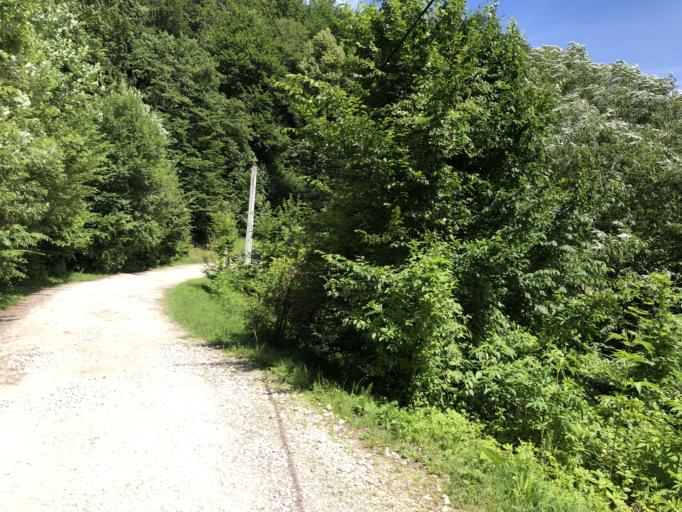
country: RO
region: Brasov
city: Brasov
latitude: 45.6264
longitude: 25.5954
